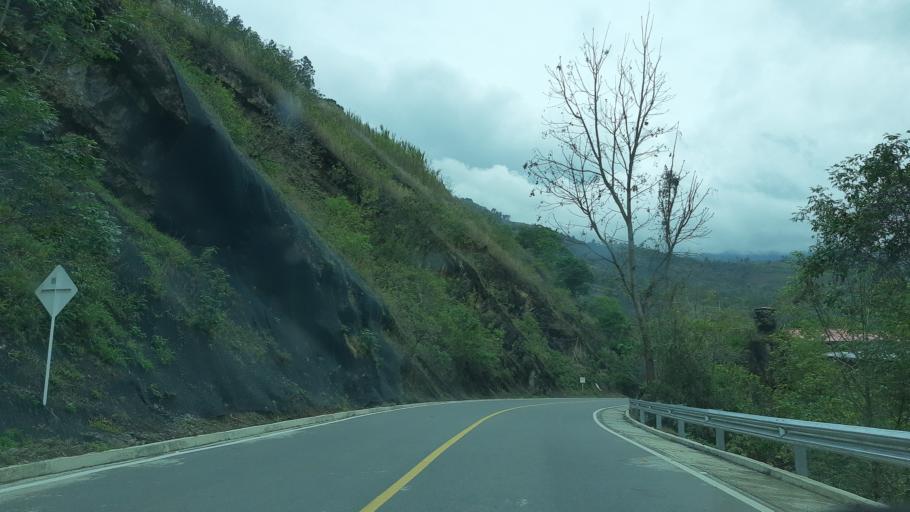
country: CO
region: Boyaca
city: Garagoa
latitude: 5.0157
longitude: -73.3692
